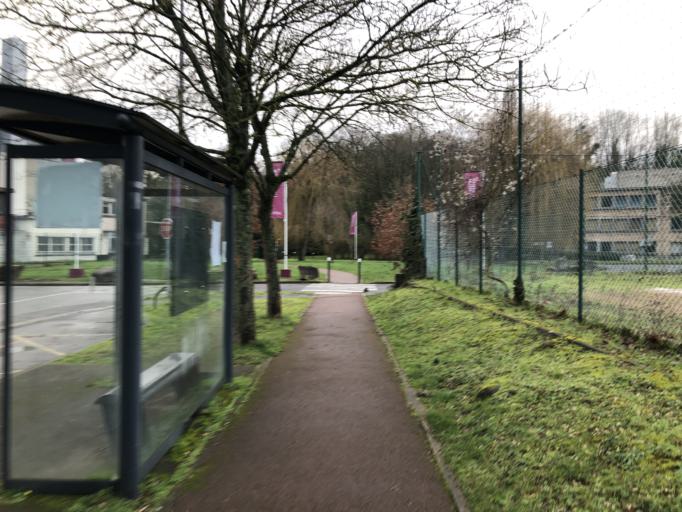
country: FR
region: Ile-de-France
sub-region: Departement de l'Essonne
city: Bures-sur-Yvette
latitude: 48.6993
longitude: 2.1674
